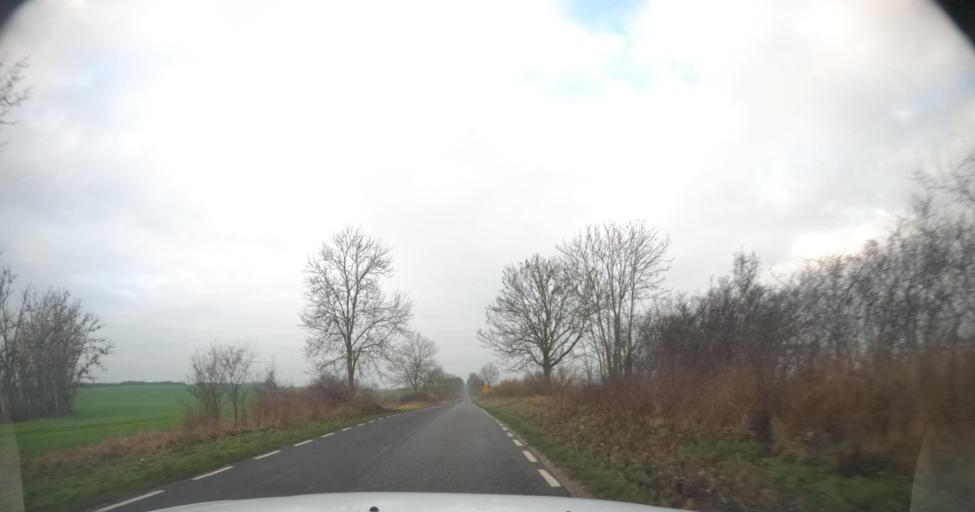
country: PL
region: West Pomeranian Voivodeship
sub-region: Powiat mysliborski
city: Debno
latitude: 52.7354
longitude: 14.6395
